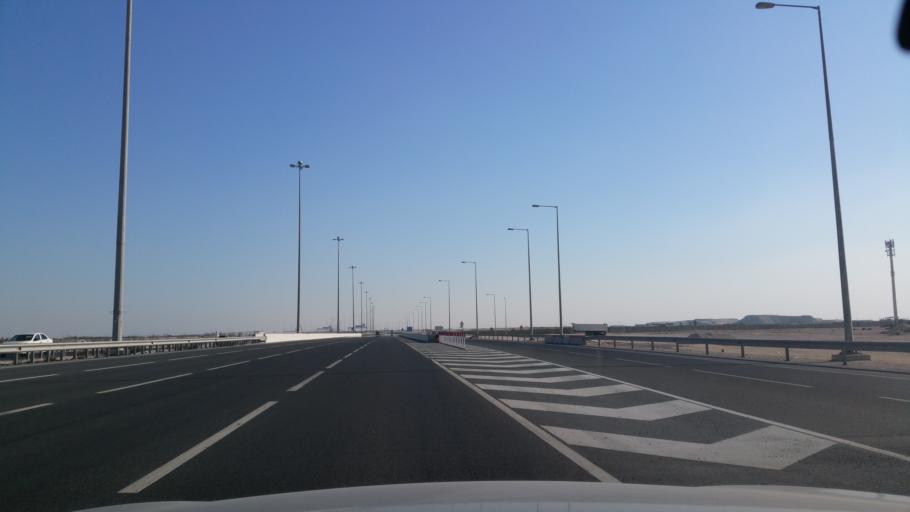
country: QA
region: Al Wakrah
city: Al Wukayr
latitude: 25.1530
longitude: 51.4735
